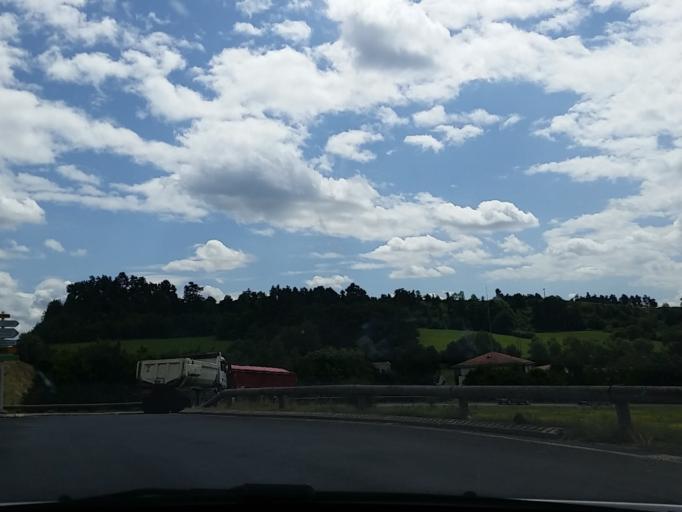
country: FR
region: Auvergne
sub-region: Departement du Cantal
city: Saint-Flour
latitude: 45.0513
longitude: 3.1100
